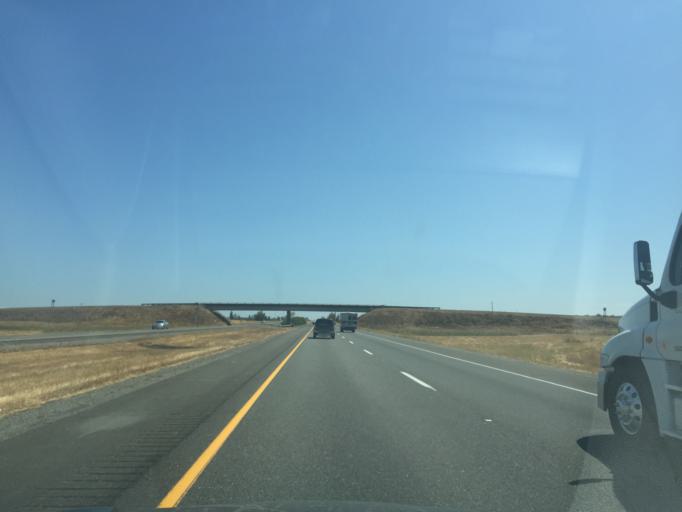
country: US
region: California
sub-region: Tehama County
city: Gerber
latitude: 40.0022
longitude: -122.2063
